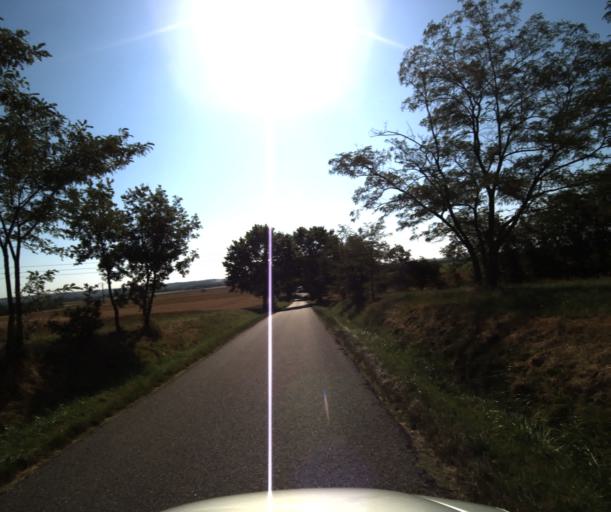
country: FR
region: Midi-Pyrenees
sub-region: Departement de la Haute-Garonne
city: Eaunes
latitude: 43.4341
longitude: 1.3738
